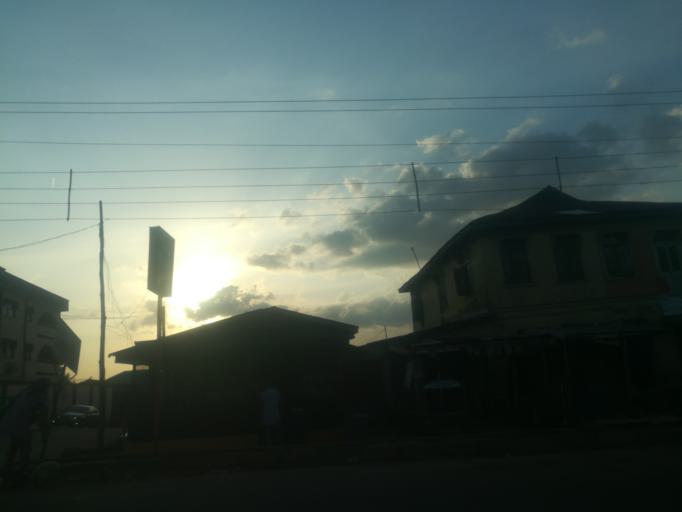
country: NG
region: Ogun
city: Abeokuta
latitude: 7.1386
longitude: 3.3388
